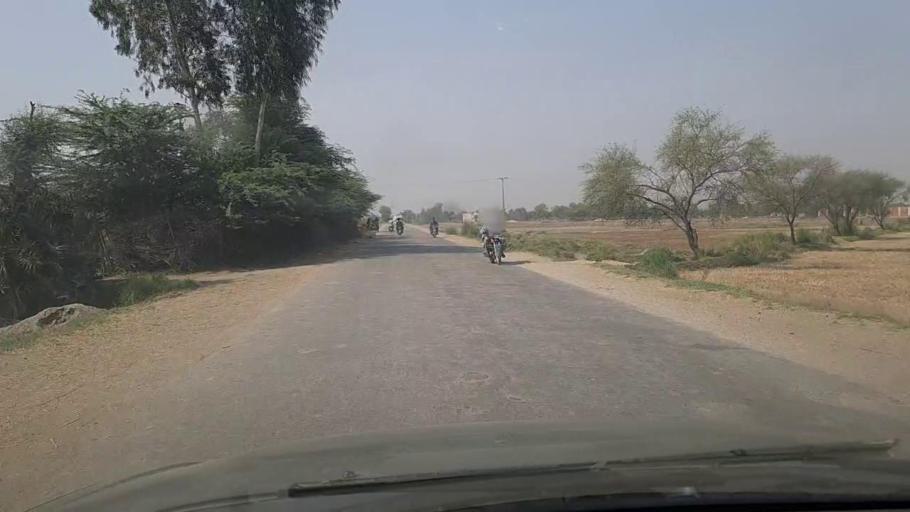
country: PK
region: Sindh
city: Mirpur Mathelo
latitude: 27.9278
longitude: 69.5319
